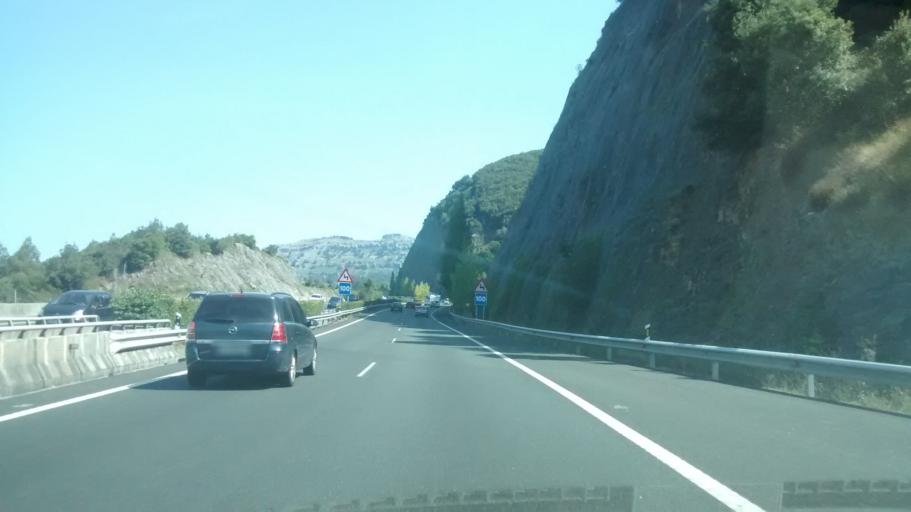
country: ES
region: Cantabria
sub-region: Provincia de Cantabria
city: Liendo
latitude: 43.3828
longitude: -3.3659
